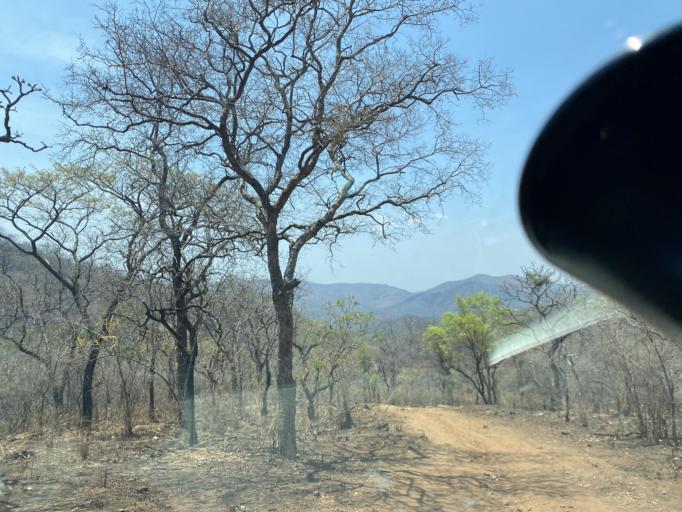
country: ZM
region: Lusaka
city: Kafue
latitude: -15.8026
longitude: 28.4496
